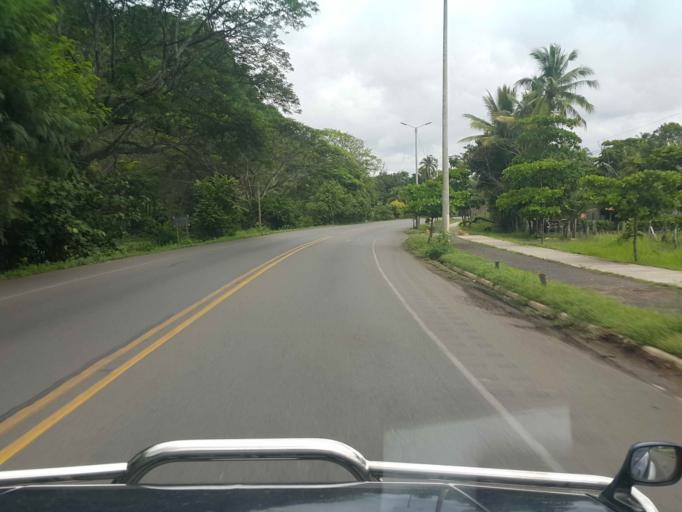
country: CR
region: Puntarenas
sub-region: Canton Central de Puntarenas
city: Chacarita
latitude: 9.9377
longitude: -84.7257
